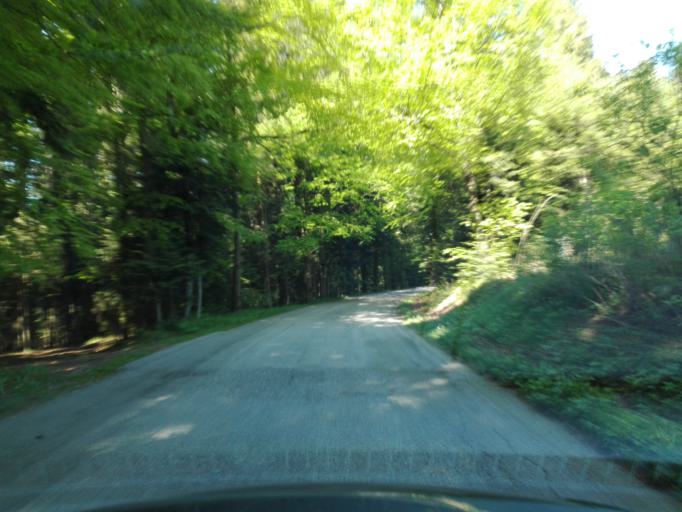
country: DE
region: Bavaria
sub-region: Lower Bavaria
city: Obernzell
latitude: 48.4358
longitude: 13.6769
